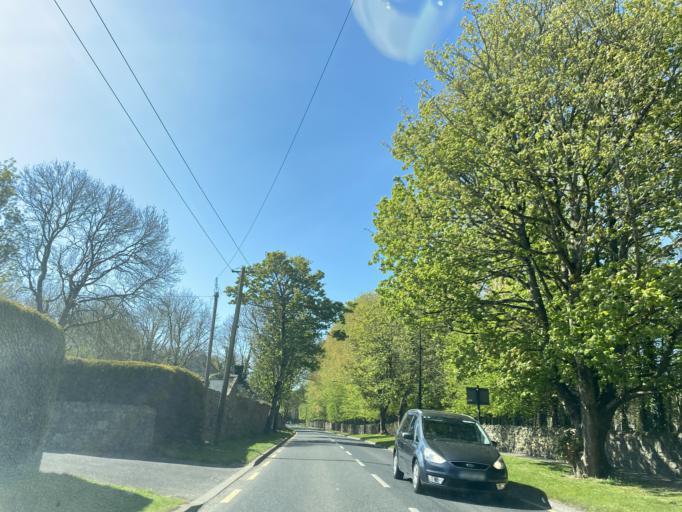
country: IE
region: Leinster
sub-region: Kildare
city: Kill
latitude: 53.3094
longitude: -6.6105
